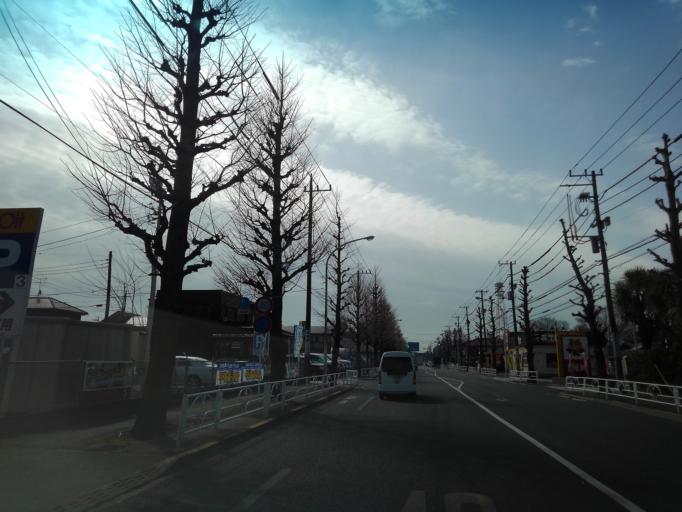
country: JP
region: Tokyo
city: Tanashicho
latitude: 35.7434
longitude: 139.5026
